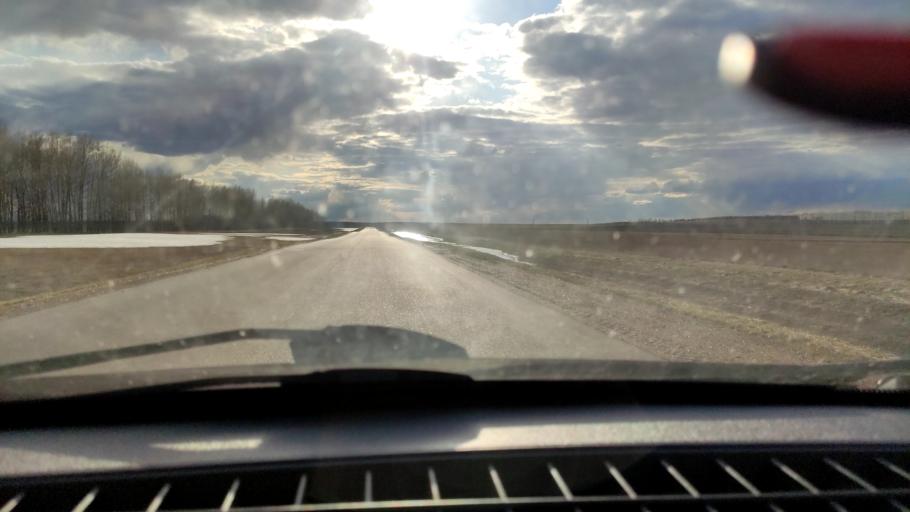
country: RU
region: Bashkortostan
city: Karmaskaly
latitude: 54.3465
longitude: 56.0348
